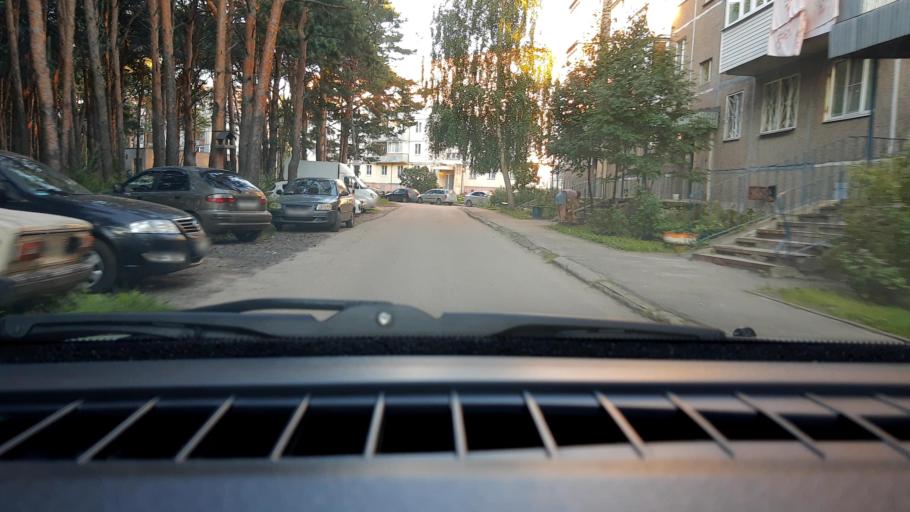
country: RU
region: Nizjnij Novgorod
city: Burevestnik
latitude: 56.1622
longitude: 43.9188
